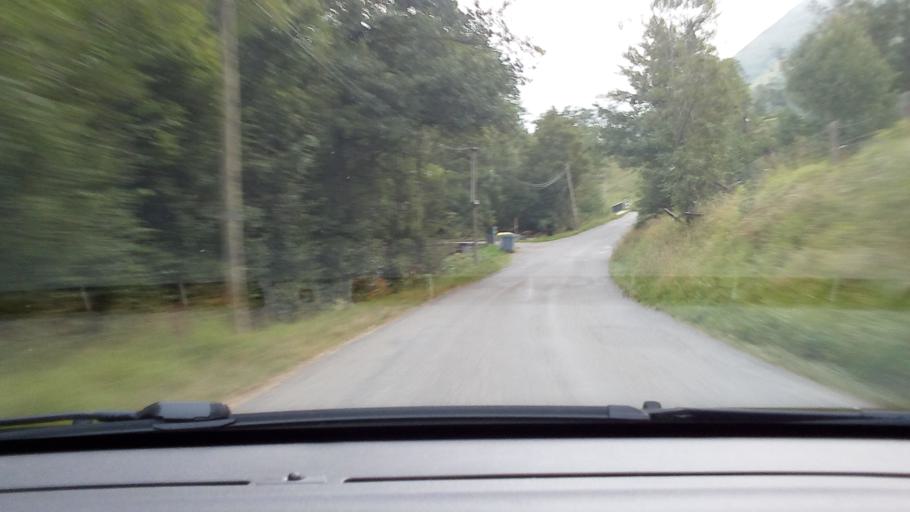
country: FR
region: Midi-Pyrenees
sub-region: Departement des Hautes-Pyrenees
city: Cauterets
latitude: 42.9225
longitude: -0.1844
